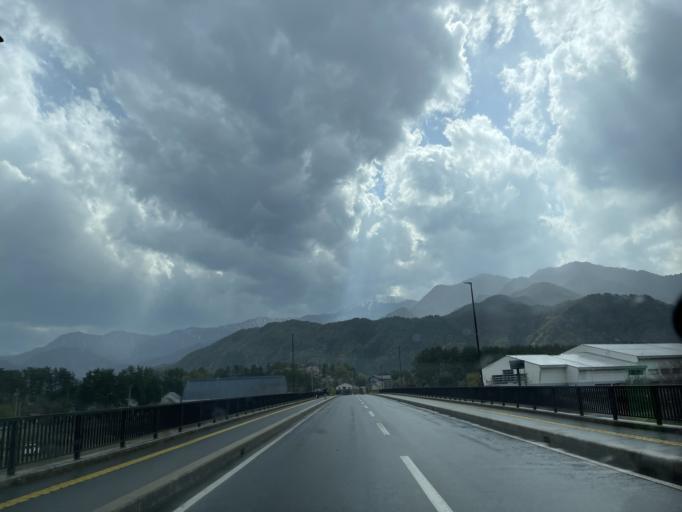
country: JP
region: Nagano
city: Omachi
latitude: 36.4979
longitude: 137.8421
